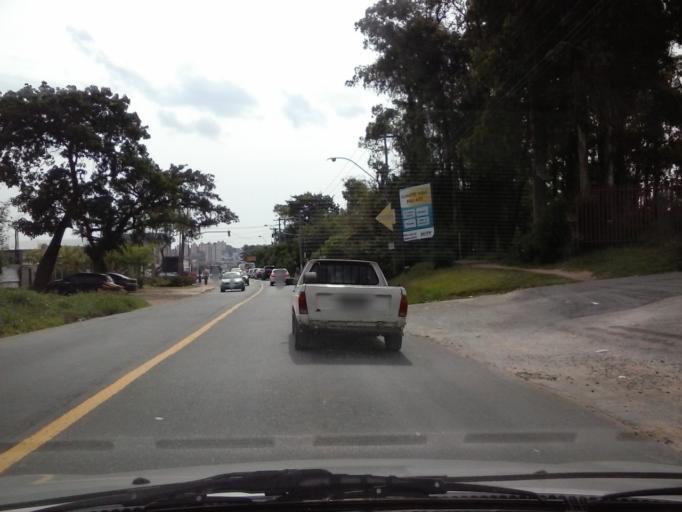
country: BR
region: Rio Grande do Sul
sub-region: Cachoeirinha
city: Cachoeirinha
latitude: -30.0381
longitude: -51.1192
